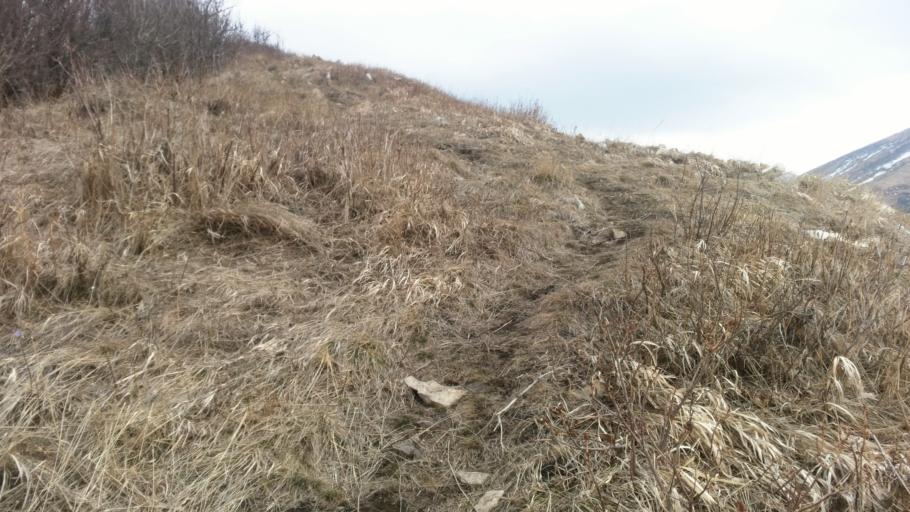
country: RU
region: Stavropol'skiy
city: Zheleznovodsk
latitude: 44.1068
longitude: 43.0160
